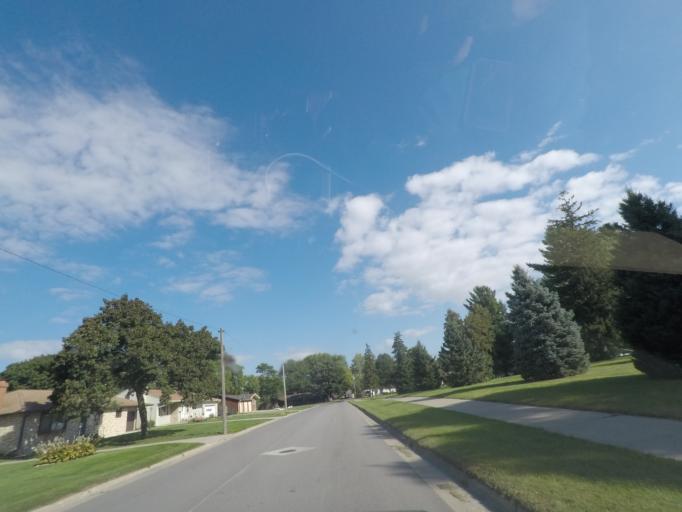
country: US
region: Iowa
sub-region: Story County
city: Nevada
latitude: 42.0180
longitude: -93.4447
